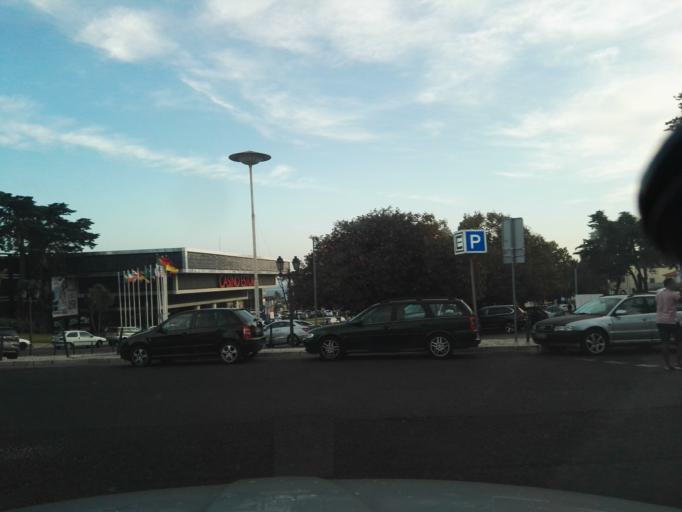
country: PT
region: Lisbon
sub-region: Cascais
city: Estoril
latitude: 38.7084
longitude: -9.3982
